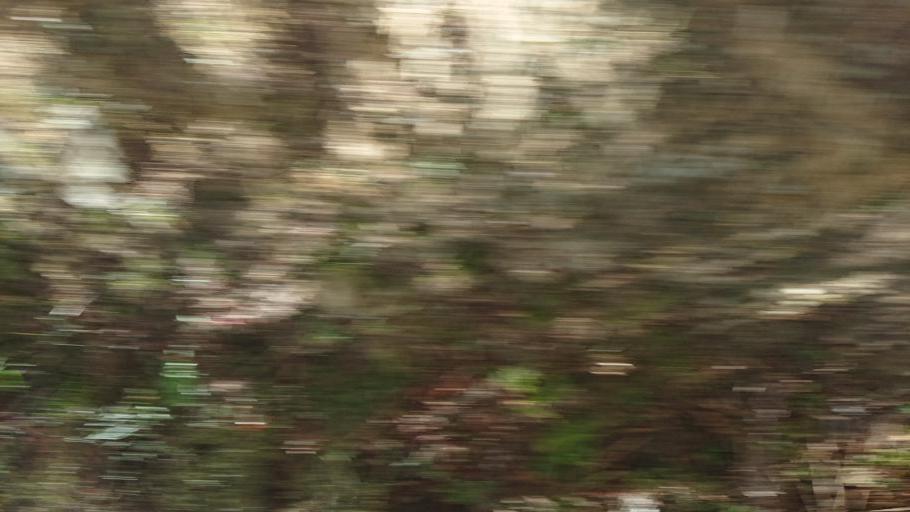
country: TW
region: Taiwan
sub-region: Hualien
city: Hualian
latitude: 24.3732
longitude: 121.3369
